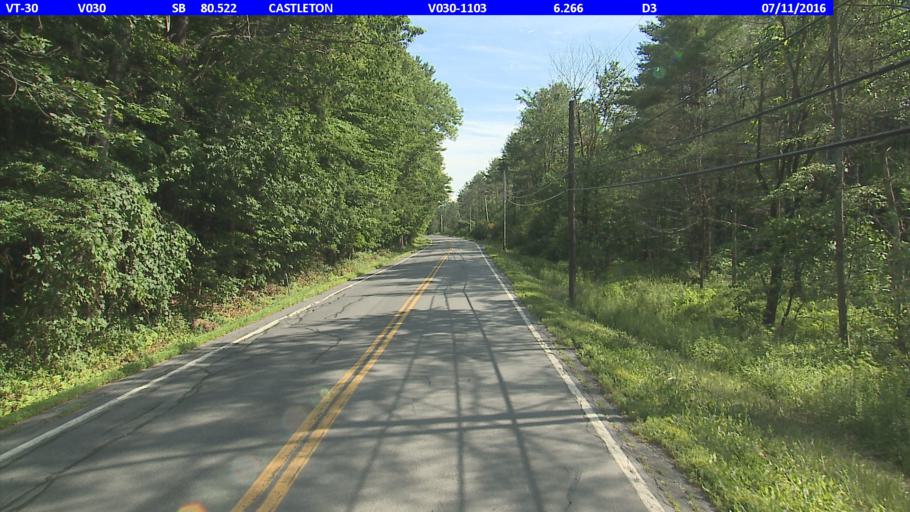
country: US
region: Vermont
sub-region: Rutland County
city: Castleton
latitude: 43.6750
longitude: -73.1915
